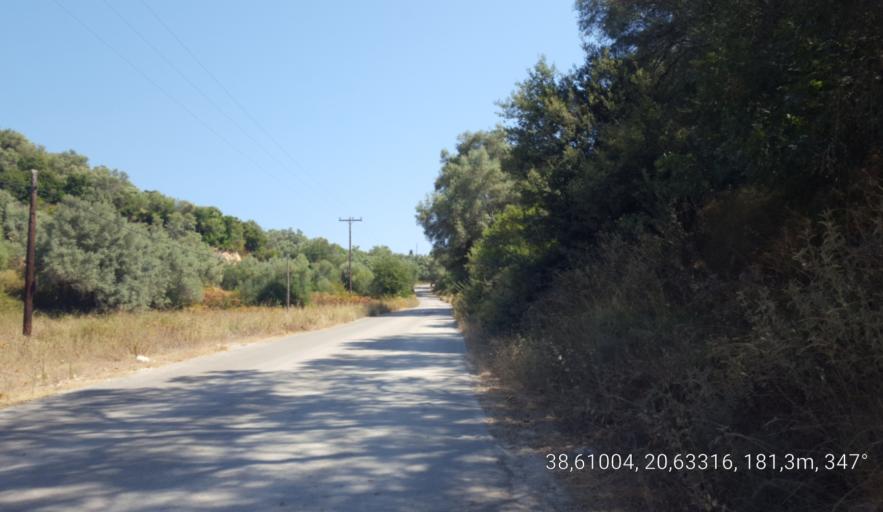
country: GR
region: Ionian Islands
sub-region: Lefkada
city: Nidri
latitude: 38.6100
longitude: 20.6331
